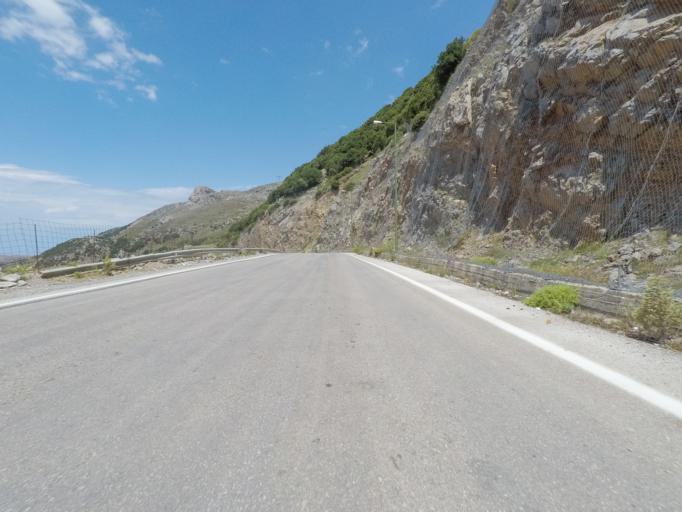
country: GR
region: Crete
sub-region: Nomos Irakleiou
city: Mokhos
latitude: 35.2067
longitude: 25.4572
